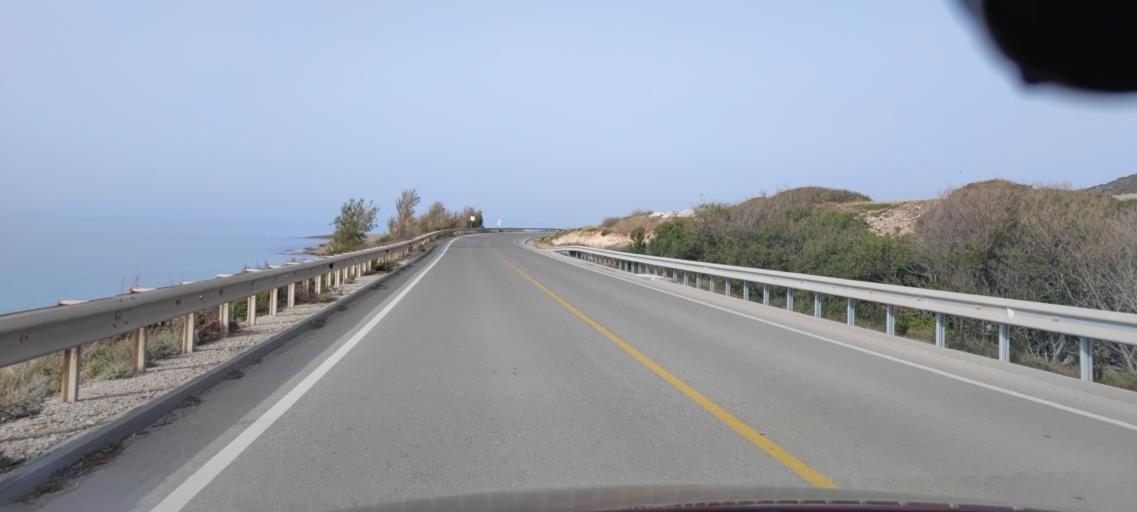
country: CY
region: Ammochostos
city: Leonarisso
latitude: 35.4723
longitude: 34.0449
